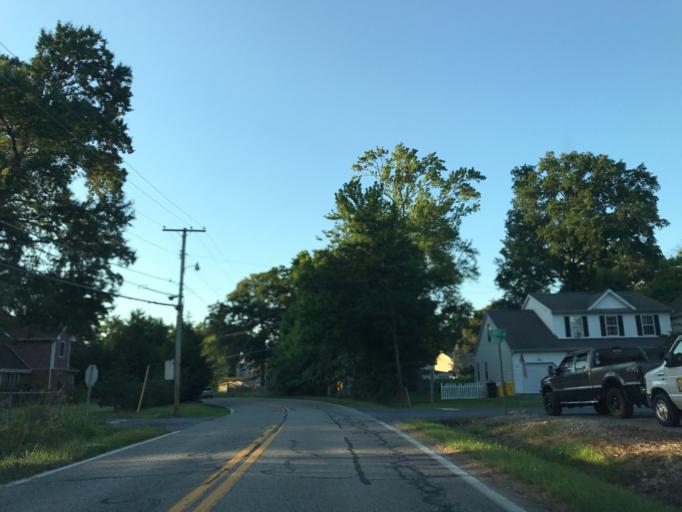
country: US
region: Maryland
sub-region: Anne Arundel County
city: Mayo
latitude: 38.8810
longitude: -76.5085
